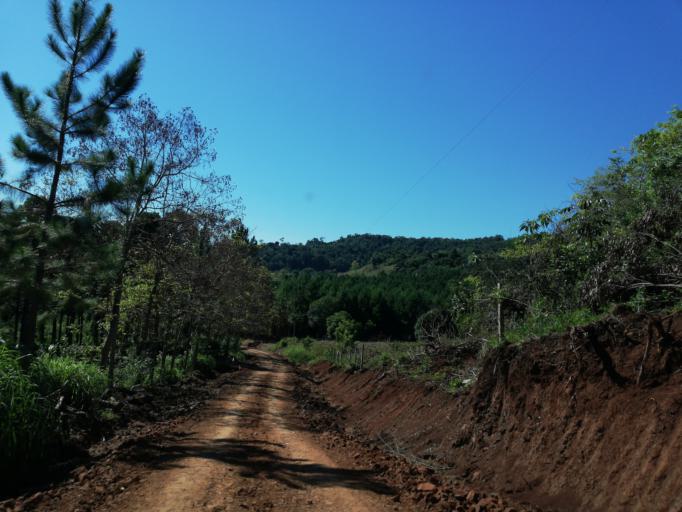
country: AR
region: Misiones
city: Dos de Mayo
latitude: -27.0718
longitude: -54.3948
